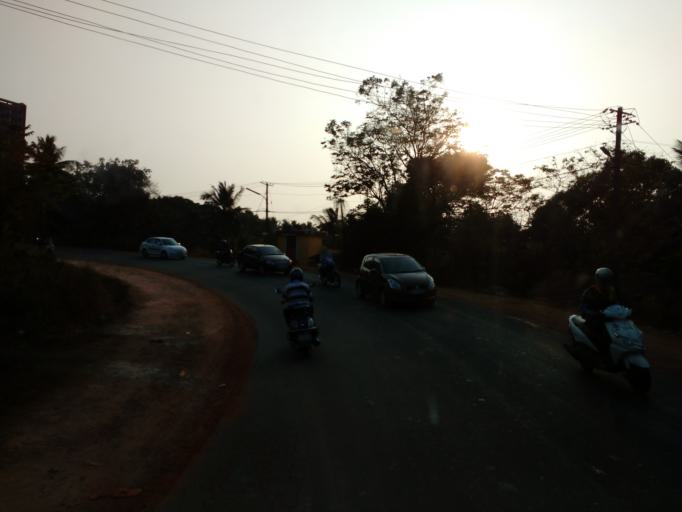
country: IN
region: Karnataka
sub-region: Dakshina Kannada
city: Mangalore
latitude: 12.8944
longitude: 74.8901
